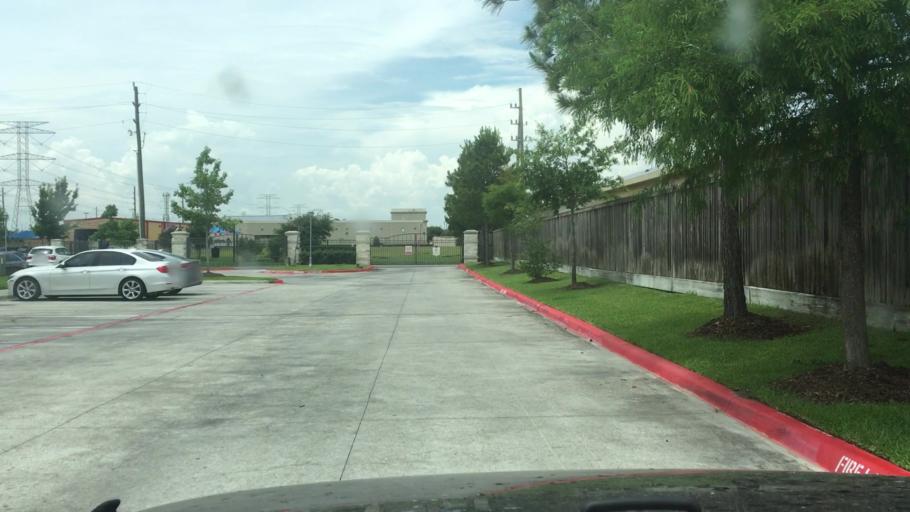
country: US
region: Texas
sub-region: Harris County
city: Humble
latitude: 29.9331
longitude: -95.2450
